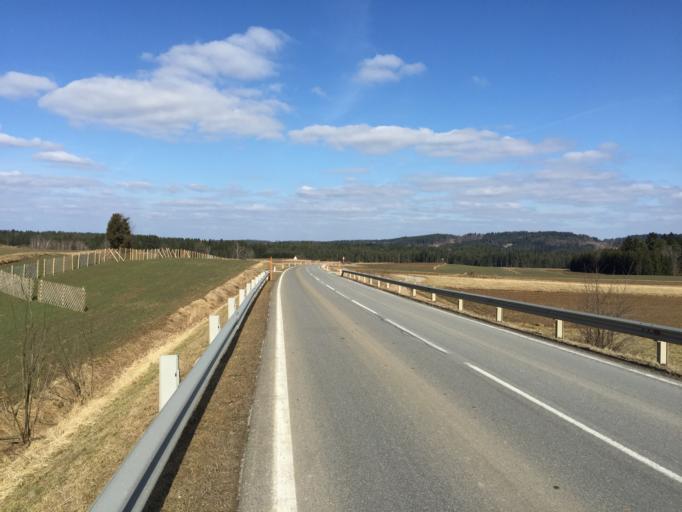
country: AT
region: Lower Austria
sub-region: Politischer Bezirk Gmund
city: Weitra
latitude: 48.6706
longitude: 14.9382
